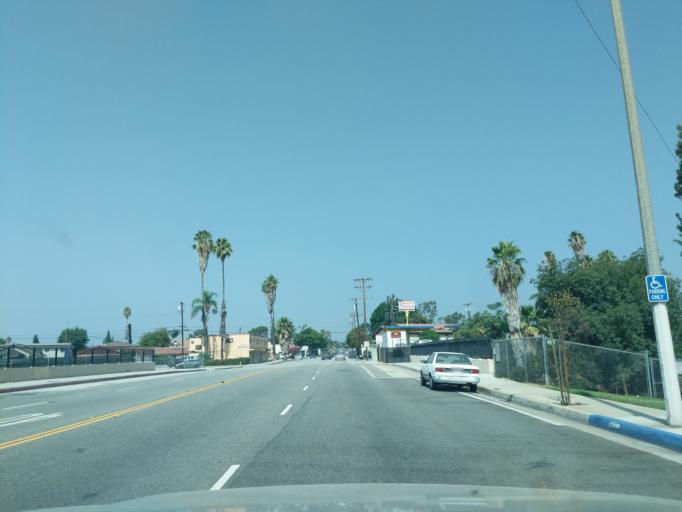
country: US
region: California
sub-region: Los Angeles County
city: East San Gabriel
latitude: 34.0897
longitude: -118.0874
